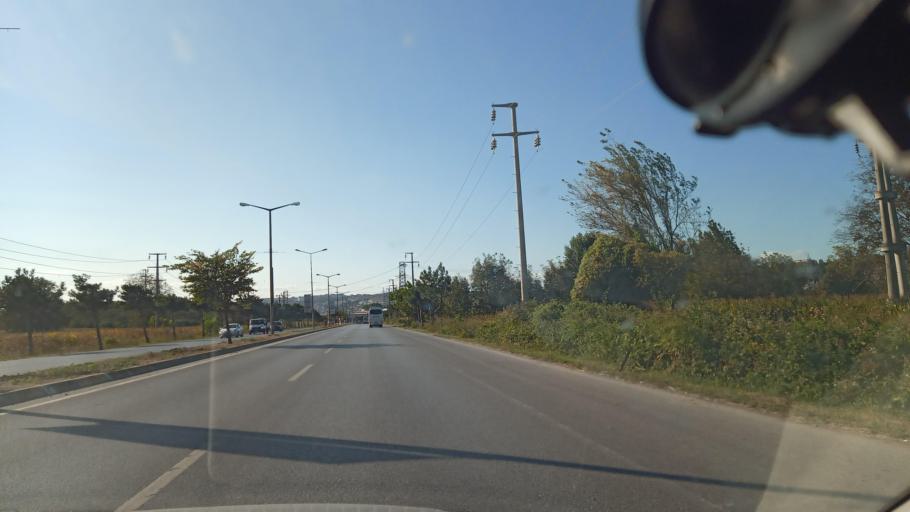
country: TR
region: Sakarya
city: Kazimpasa
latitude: 40.8411
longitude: 30.3388
